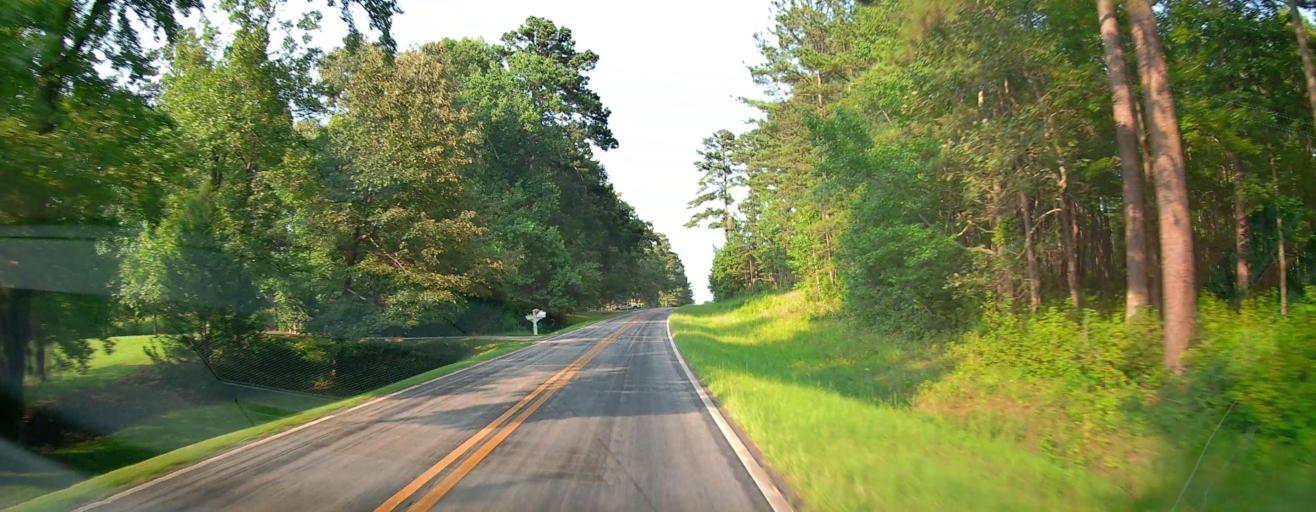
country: US
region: Georgia
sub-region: Jones County
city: Gray
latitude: 33.1002
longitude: -83.6753
